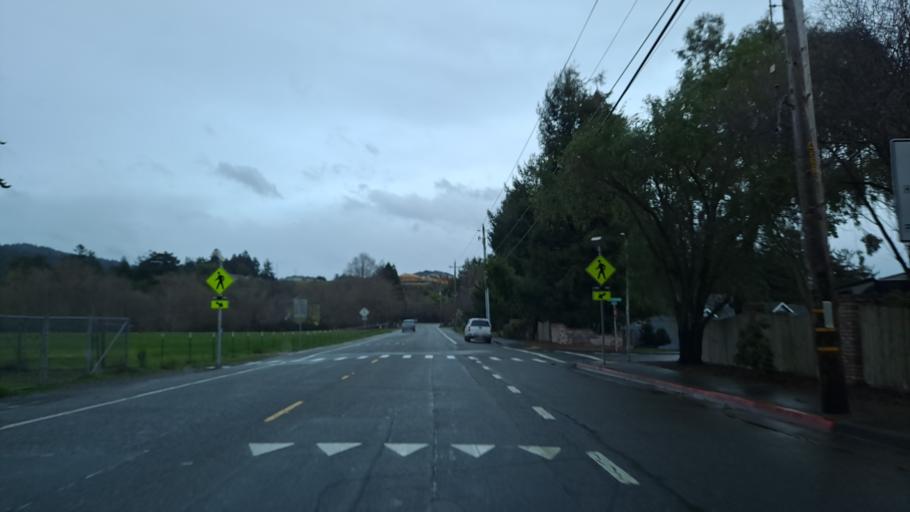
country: US
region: California
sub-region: Humboldt County
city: Fortuna
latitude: 40.5907
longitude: -124.1362
